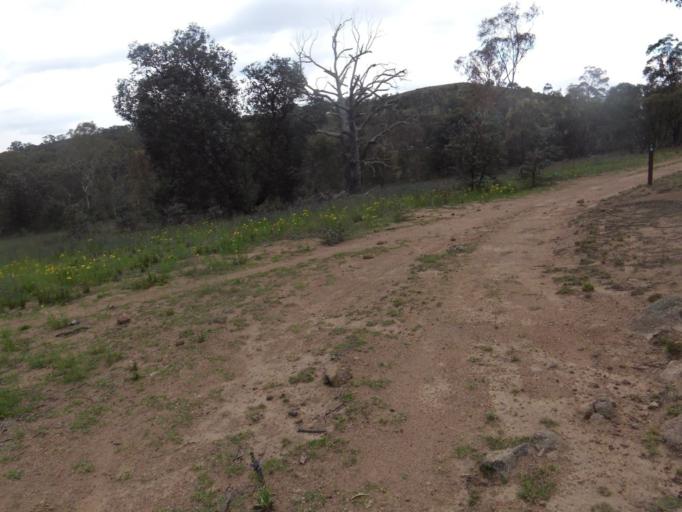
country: AU
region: Australian Capital Territory
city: Forrest
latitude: -35.3495
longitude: 149.1228
